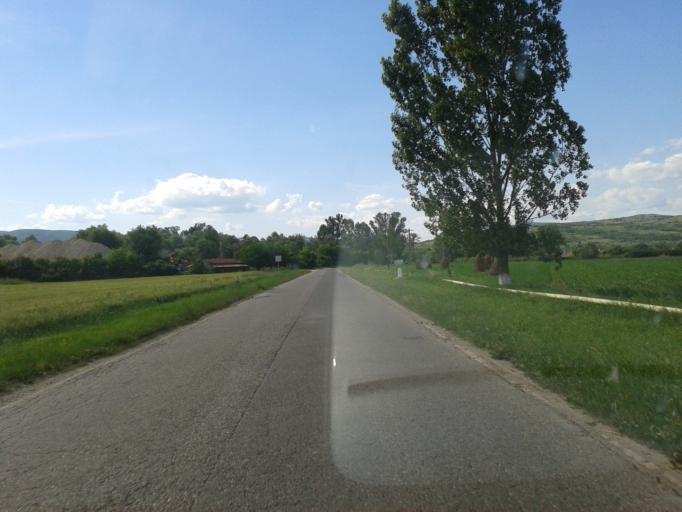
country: RO
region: Hunedoara
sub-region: Comuna Geoagiu
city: Geoagiu
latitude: 45.8930
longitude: 23.2282
